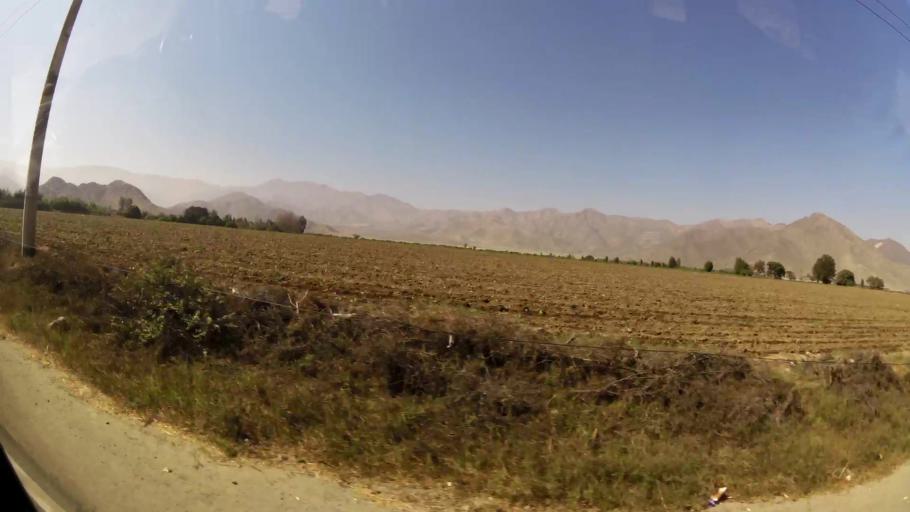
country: PE
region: Ica
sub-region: Provincia de Ica
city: San Juan Bautista
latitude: -13.9426
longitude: -75.6778
